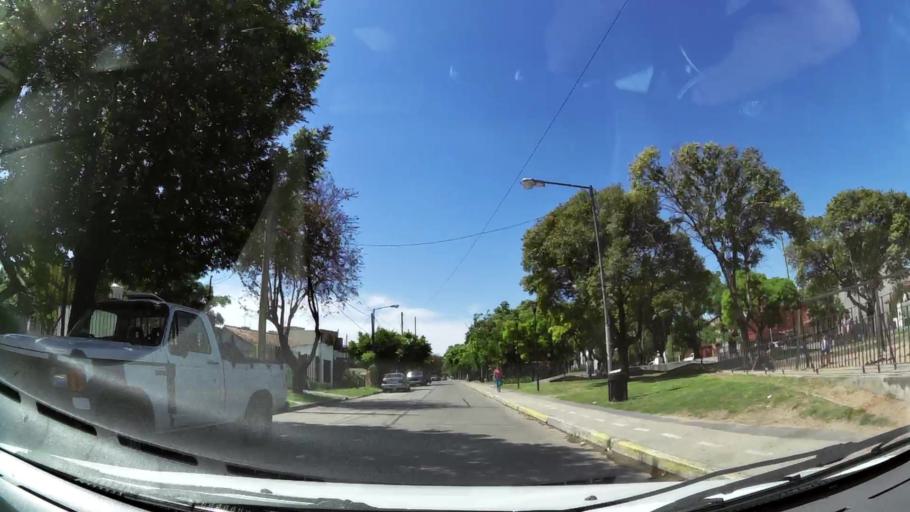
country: AR
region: Buenos Aires
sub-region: Partido de General San Martin
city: General San Martin
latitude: -34.5646
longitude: -58.5509
